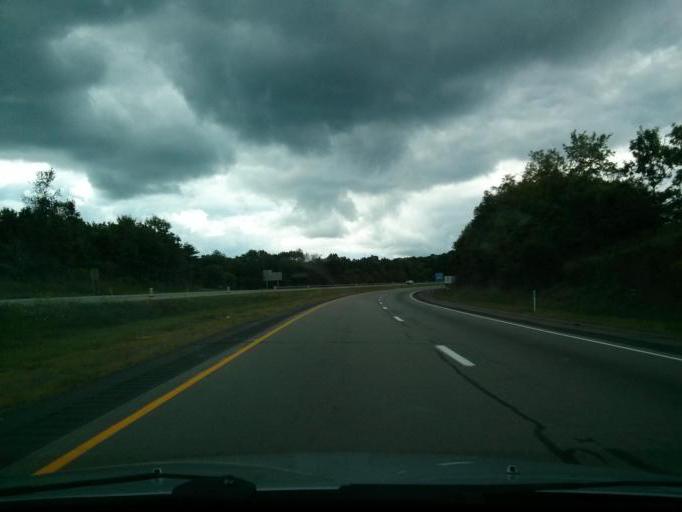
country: US
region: Pennsylvania
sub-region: Clarion County
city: Clarion
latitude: 41.1816
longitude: -79.2457
